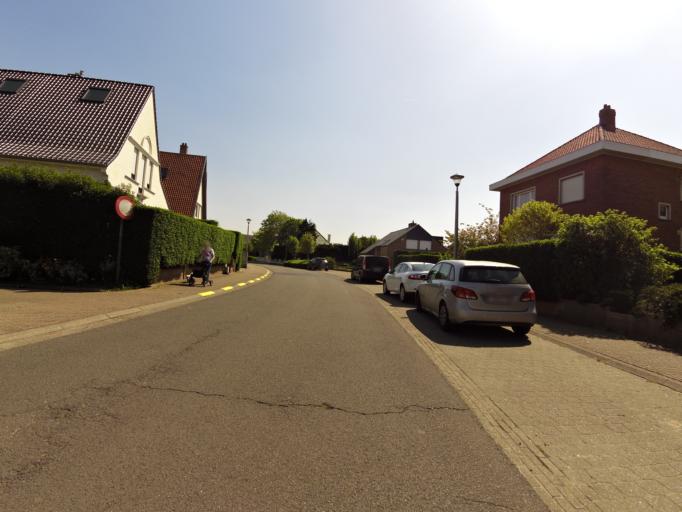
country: BE
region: Flanders
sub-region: Provincie West-Vlaanderen
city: Middelkerke
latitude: 51.1849
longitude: 2.8162
